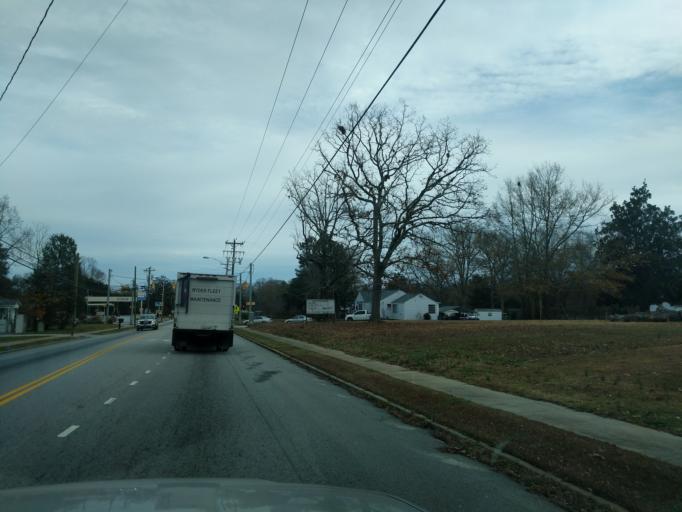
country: US
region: South Carolina
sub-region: Anderson County
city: Williamston
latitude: 34.6470
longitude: -82.4806
